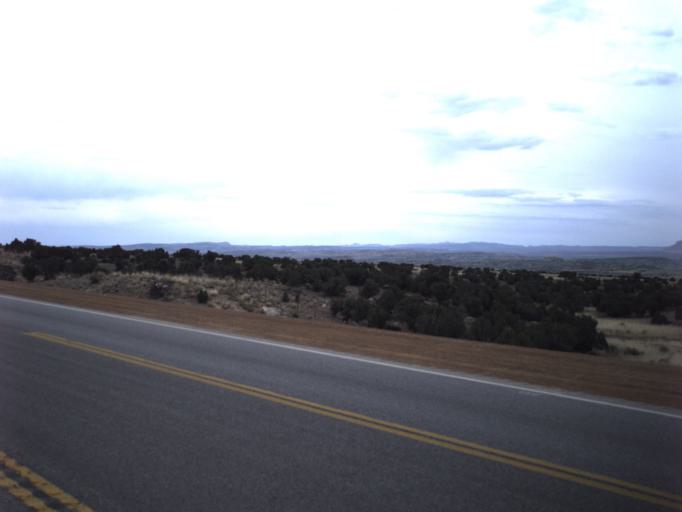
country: US
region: Utah
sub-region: Carbon County
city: East Carbon City
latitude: 39.4125
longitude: -110.4335
